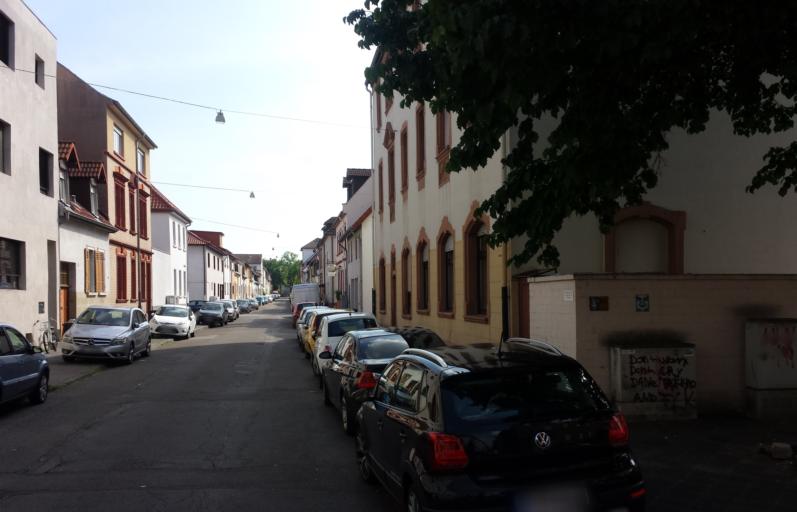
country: DE
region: Rheinland-Pfalz
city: Altrip
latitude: 49.4576
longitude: 8.4873
